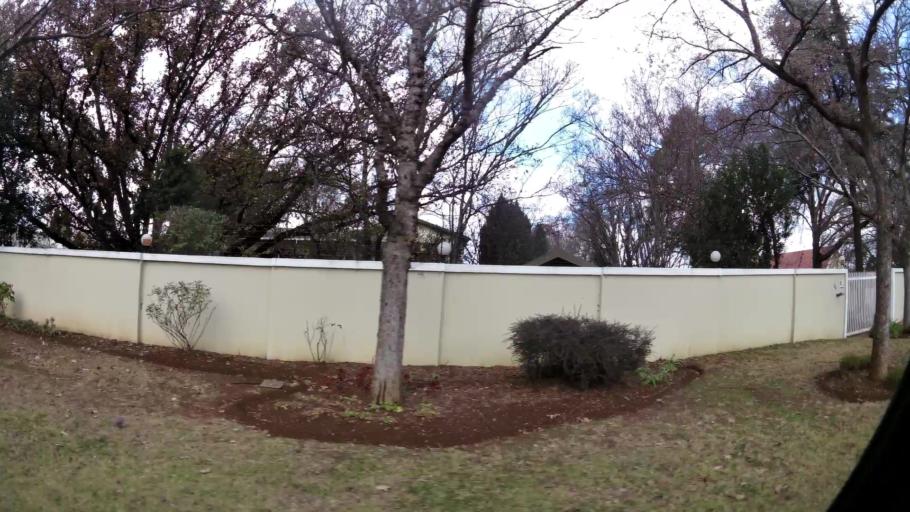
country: ZA
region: Gauteng
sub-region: Sedibeng District Municipality
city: Vanderbijlpark
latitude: -26.7422
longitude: 27.8325
